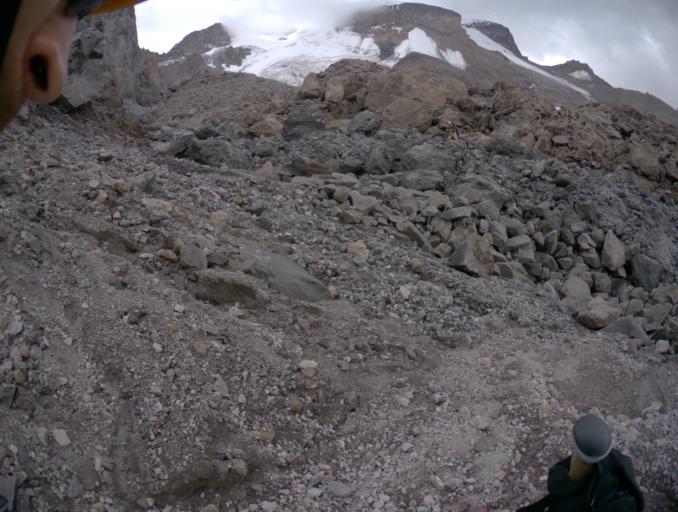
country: RU
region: Kabardino-Balkariya
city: Terskol
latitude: 43.3806
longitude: 42.3950
